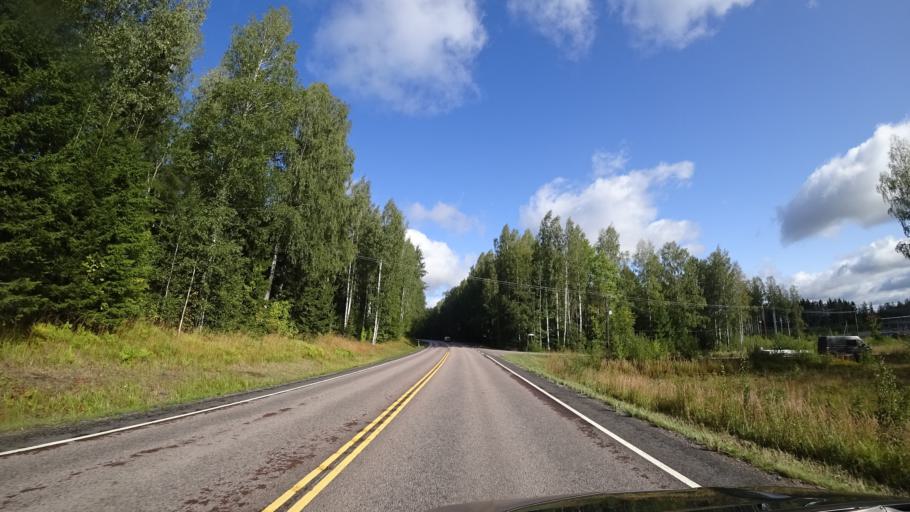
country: FI
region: Uusimaa
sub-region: Helsinki
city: Tuusula
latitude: 60.4932
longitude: 24.9387
